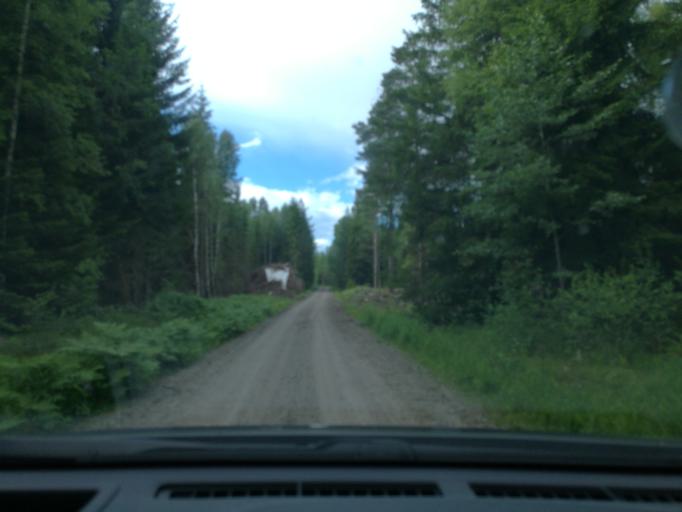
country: SE
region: Vaestmanland
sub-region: Surahammars Kommun
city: Ramnas
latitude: 59.8241
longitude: 16.2556
